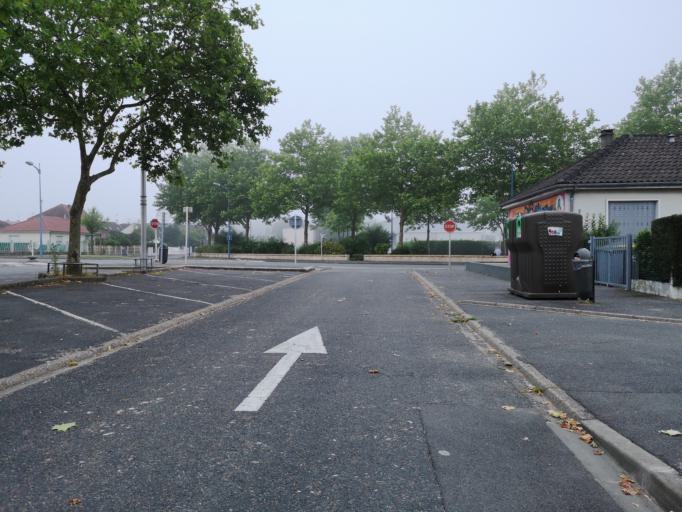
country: FR
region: Centre
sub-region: Departement du Loiret
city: Fleury-les-Aubrais
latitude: 47.9325
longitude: 1.9209
